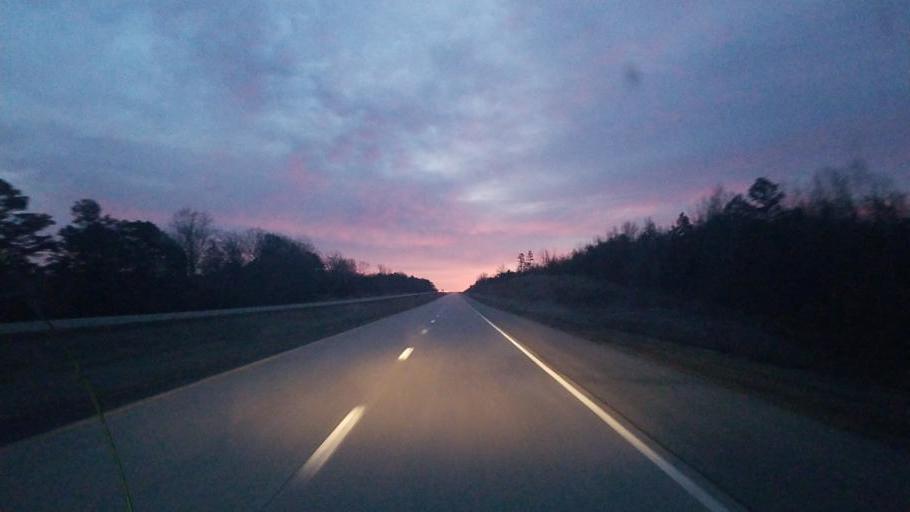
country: US
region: Missouri
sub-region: Shannon County
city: Winona
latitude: 36.9988
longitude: -91.4170
